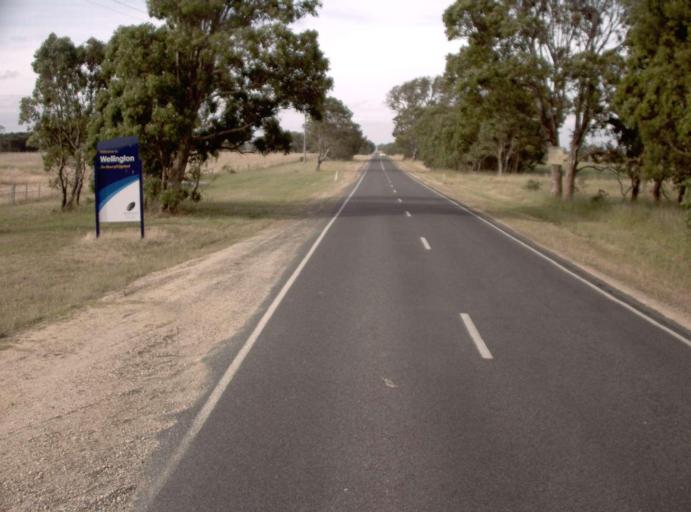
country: AU
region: Victoria
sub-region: Wellington
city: Heyfield
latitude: -38.0542
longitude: 146.6631
